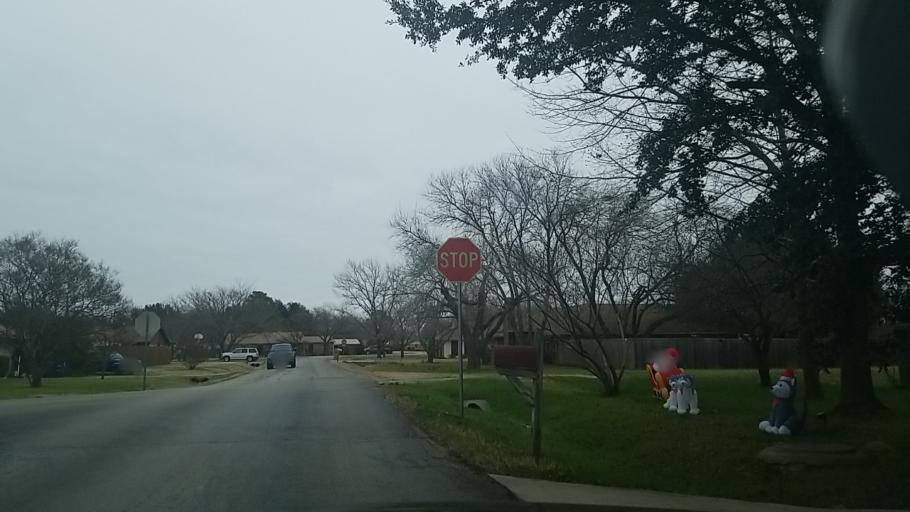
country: US
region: Texas
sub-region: Denton County
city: Corinth
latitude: 33.1490
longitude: -97.0677
